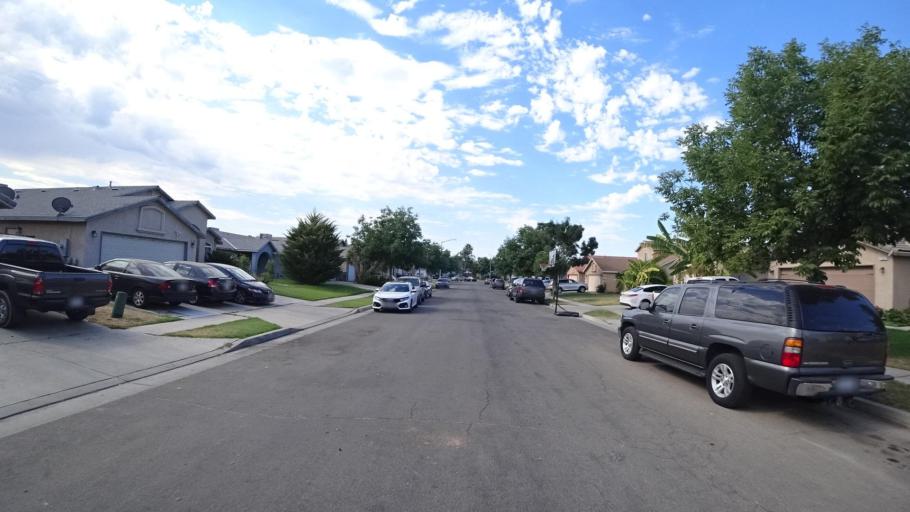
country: US
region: California
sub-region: Fresno County
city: Sunnyside
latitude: 36.7603
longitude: -119.7142
